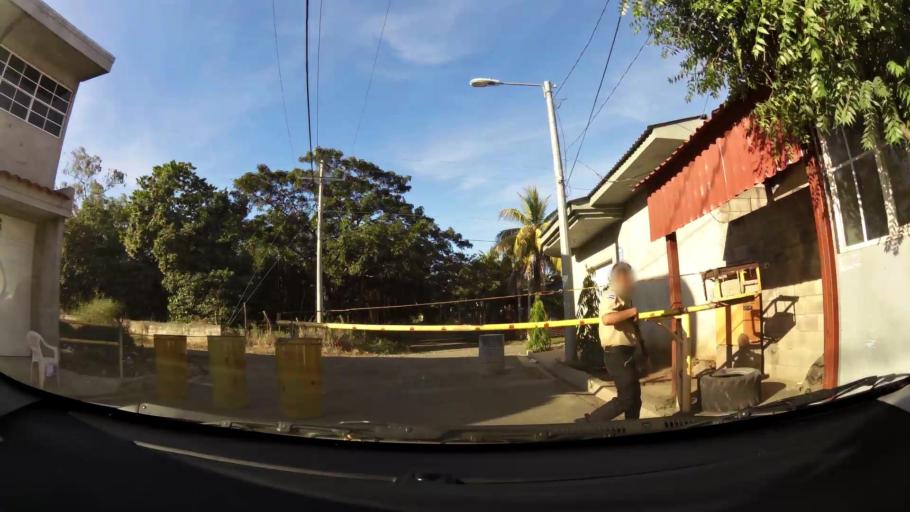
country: SV
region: San Miguel
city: San Miguel
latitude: 13.4600
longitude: -88.1688
